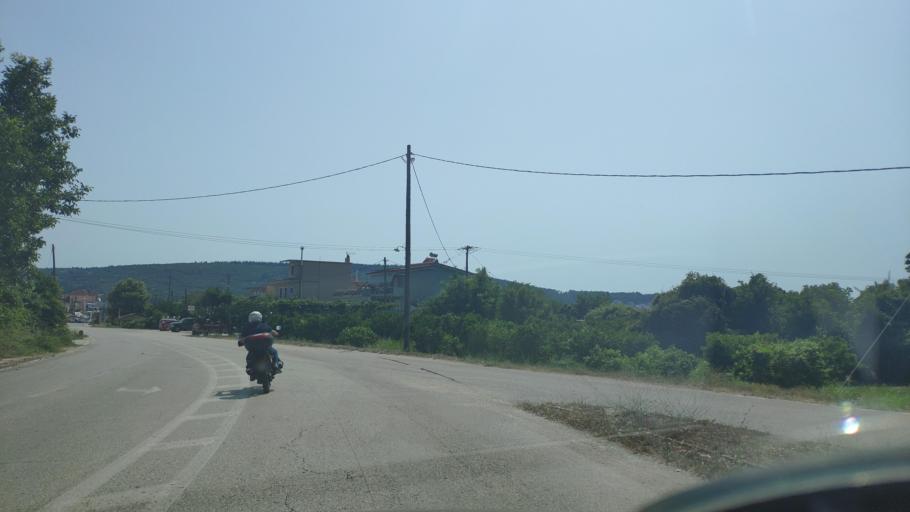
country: GR
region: Epirus
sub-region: Nomos Artas
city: Peta
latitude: 39.1642
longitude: 21.0153
